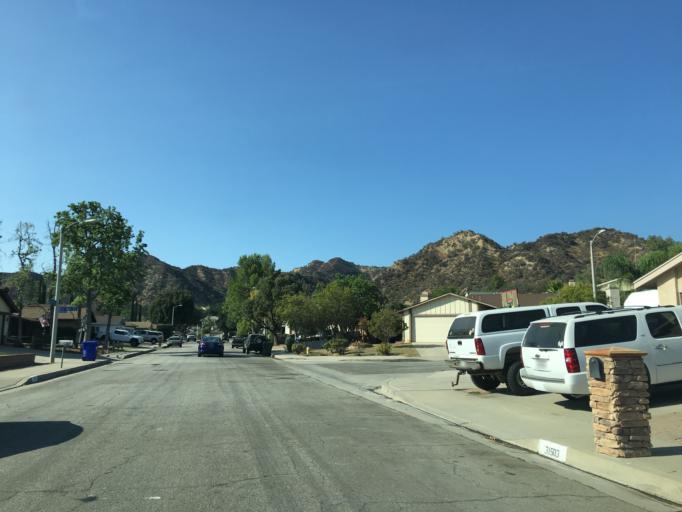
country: US
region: California
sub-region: Los Angeles County
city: Castaic
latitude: 34.4917
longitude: -118.6266
